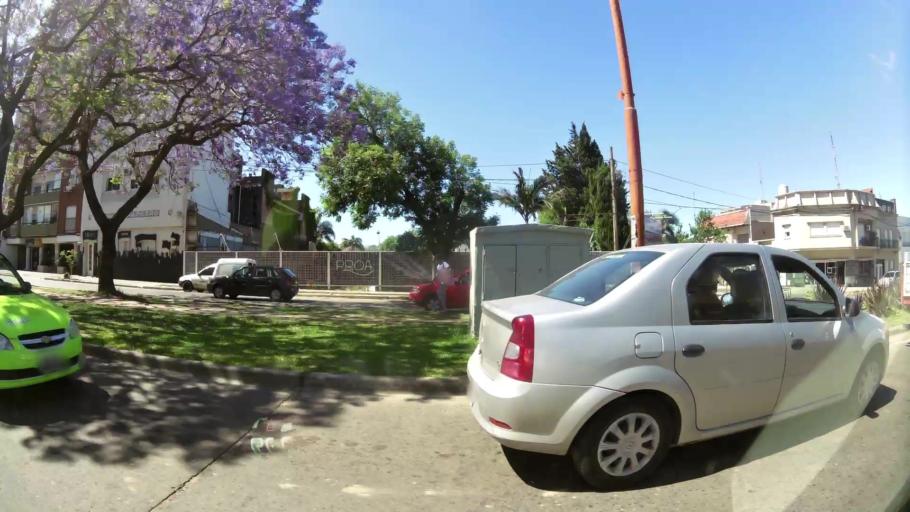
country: AR
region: Santa Fe
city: Santa Fe de la Vera Cruz
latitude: -31.6396
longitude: -60.6848
